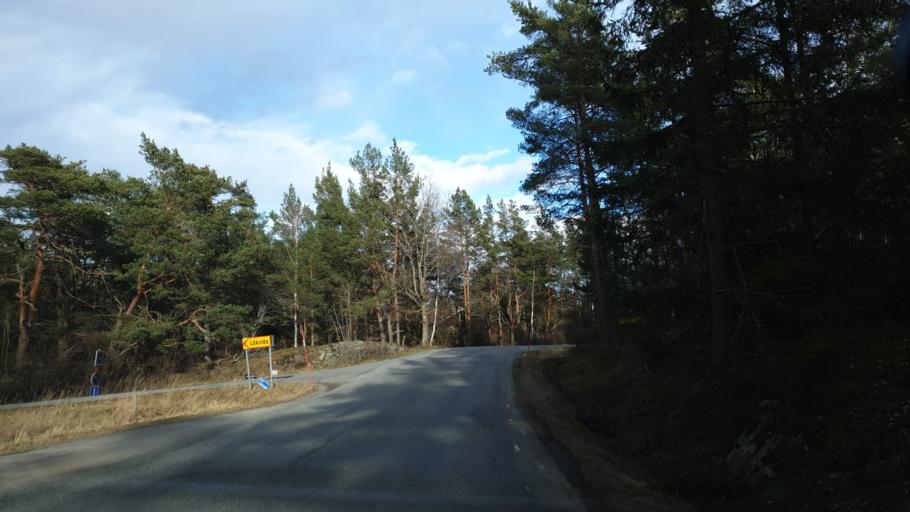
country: SE
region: Stockholm
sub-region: Varmdo Kommun
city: Holo
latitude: 59.3639
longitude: 18.6721
